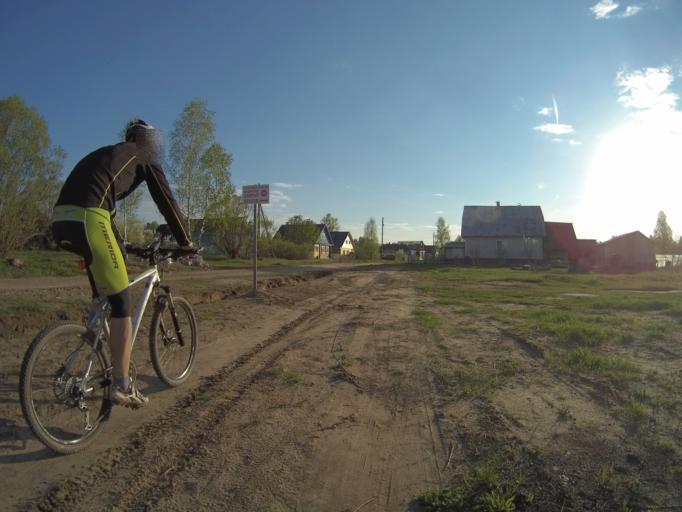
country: RU
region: Vladimir
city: Orgtrud
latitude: 56.0737
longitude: 40.7415
